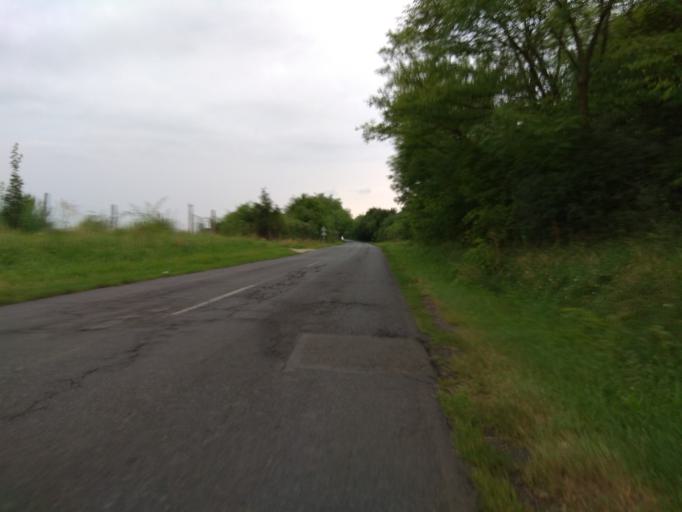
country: HU
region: Borsod-Abauj-Zemplen
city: Monok
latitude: 48.1750
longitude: 21.1080
